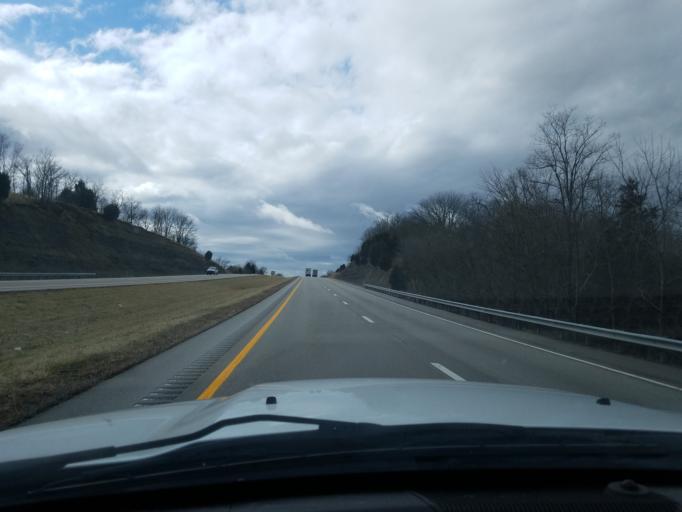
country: US
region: Kentucky
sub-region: Bath County
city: Owingsville
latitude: 38.0994
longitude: -83.8513
